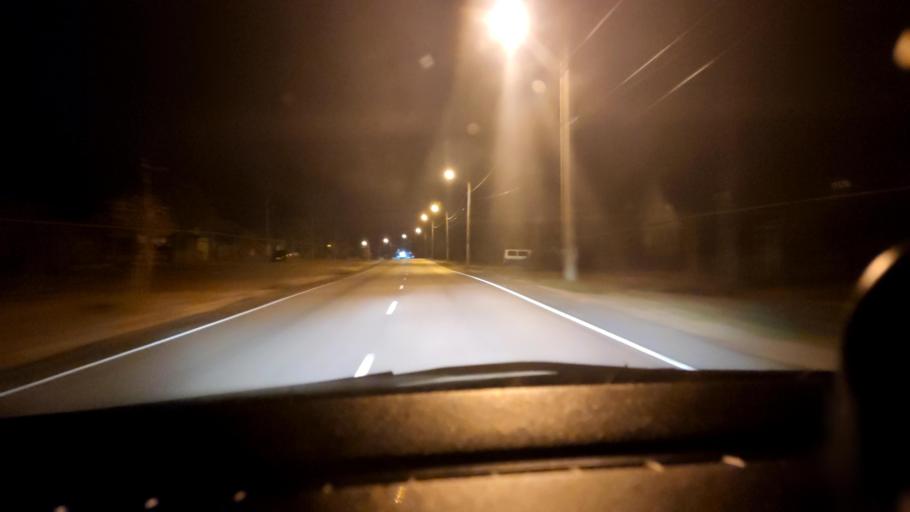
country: RU
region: Voronezj
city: Shilovo
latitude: 51.5556
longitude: 39.0635
